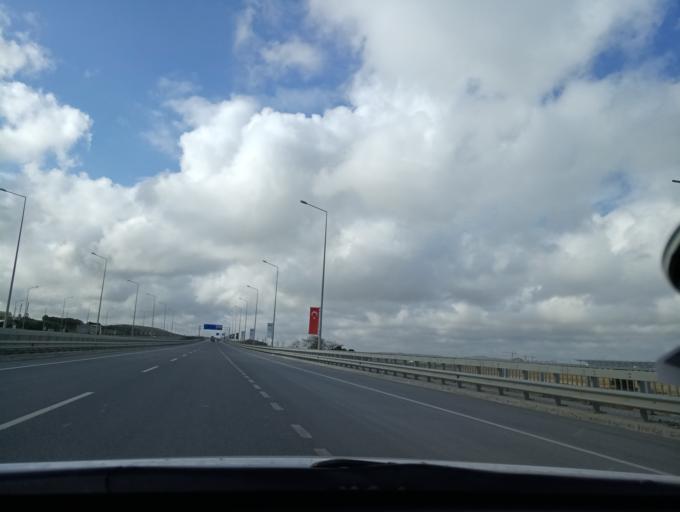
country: TR
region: Istanbul
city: Durusu
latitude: 41.2454
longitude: 28.7641
